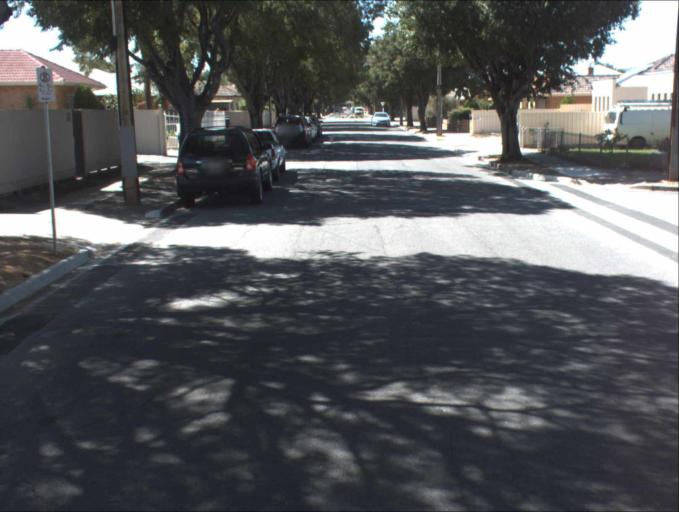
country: AU
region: South Australia
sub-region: Port Adelaide Enfield
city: Klemzig
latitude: -34.8789
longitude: 138.6360
